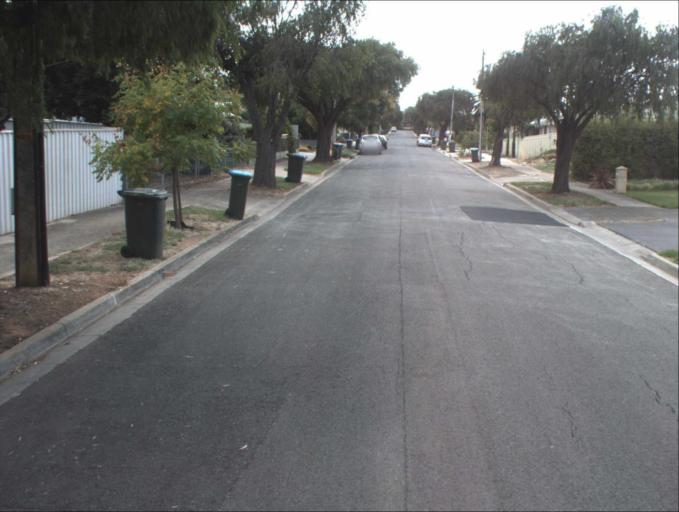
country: AU
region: South Australia
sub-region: Port Adelaide Enfield
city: Gilles Plains
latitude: -34.8530
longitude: 138.6580
